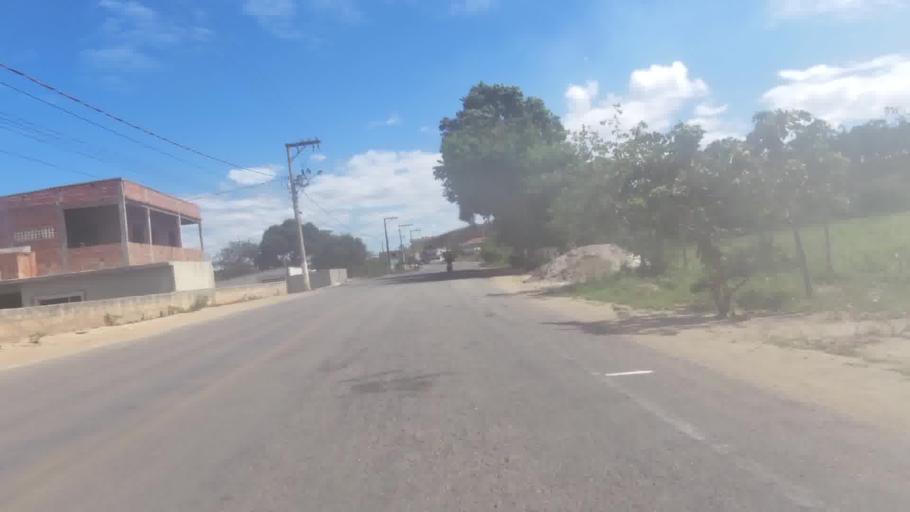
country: BR
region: Espirito Santo
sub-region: Marataizes
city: Marataizes
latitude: -21.1994
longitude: -40.9610
